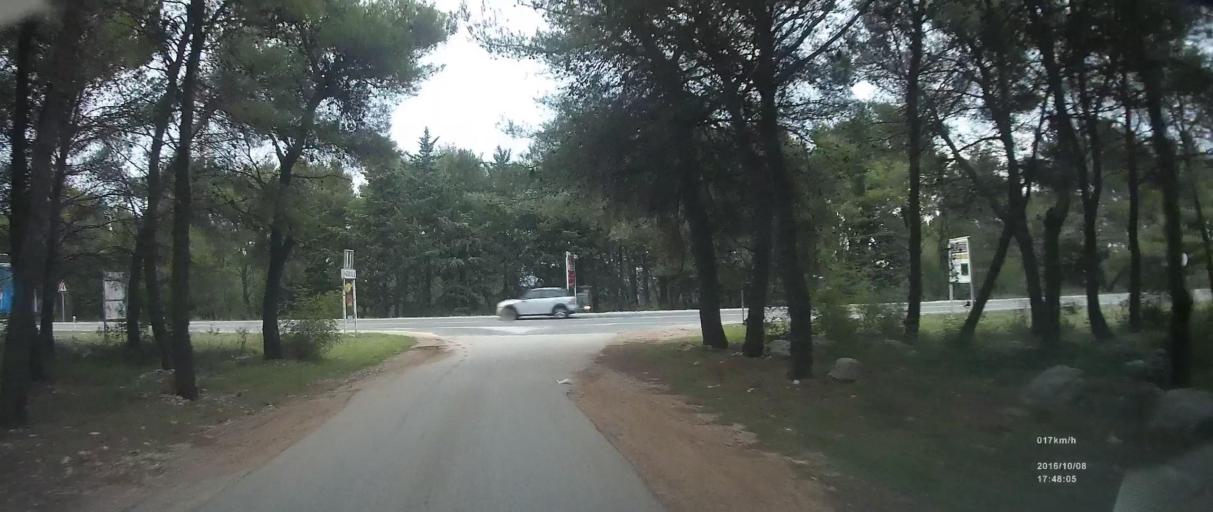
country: HR
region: Zadarska
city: Pakostane
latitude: 43.9162
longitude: 15.5056
